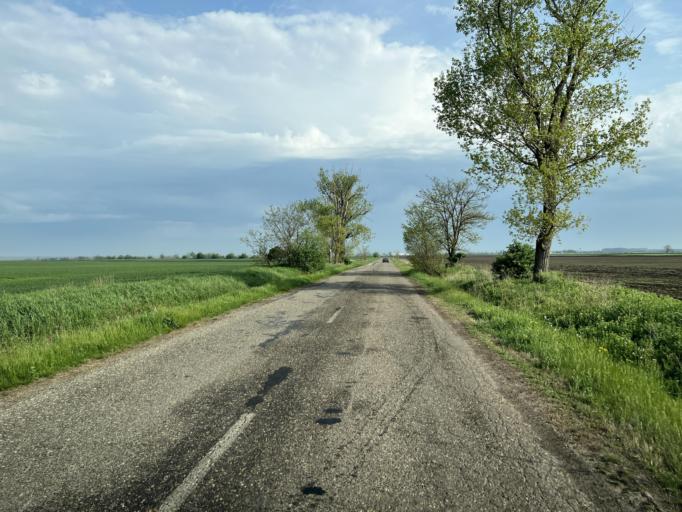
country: HU
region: Pest
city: Tapioszentmarton
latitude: 47.2850
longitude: 19.7636
